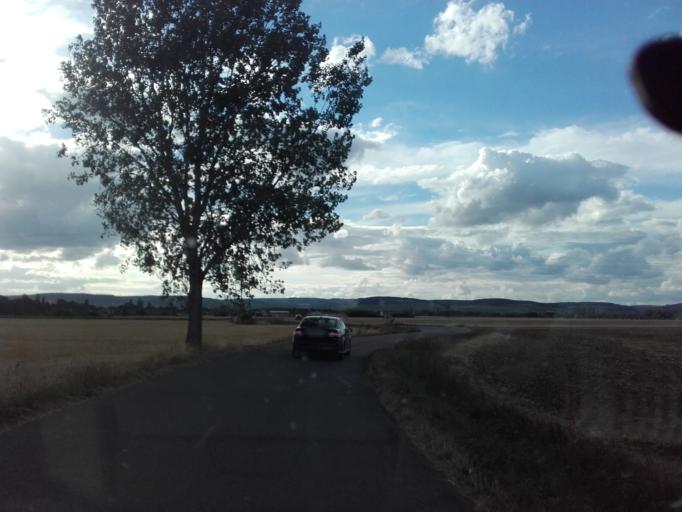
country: FR
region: Bourgogne
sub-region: Departement de la Cote-d'Or
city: Bligny-les-Beaune
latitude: 46.9876
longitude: 4.8394
